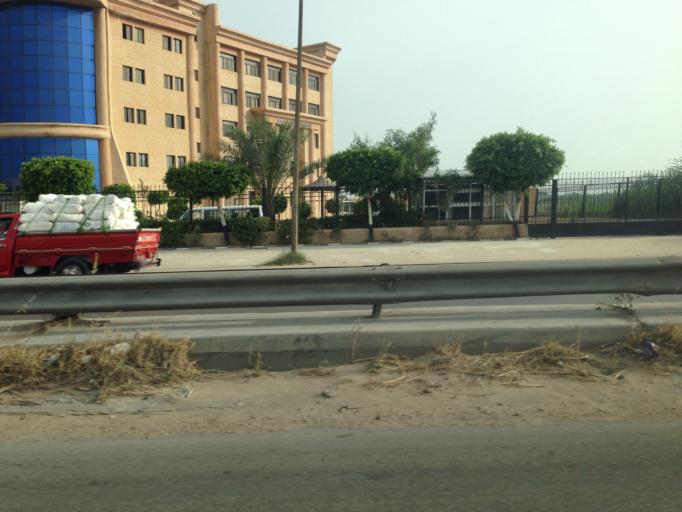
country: EG
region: Alexandria
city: Alexandria
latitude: 31.2021
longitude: 30.0188
